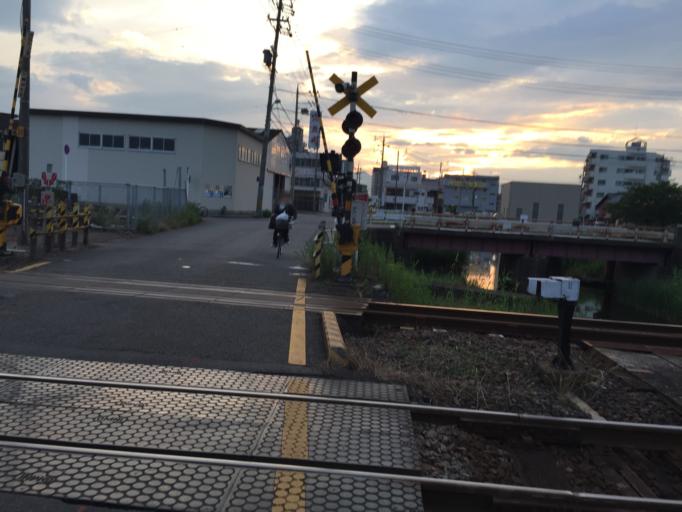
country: JP
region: Mie
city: Yokkaichi
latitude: 34.9591
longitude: 136.6284
